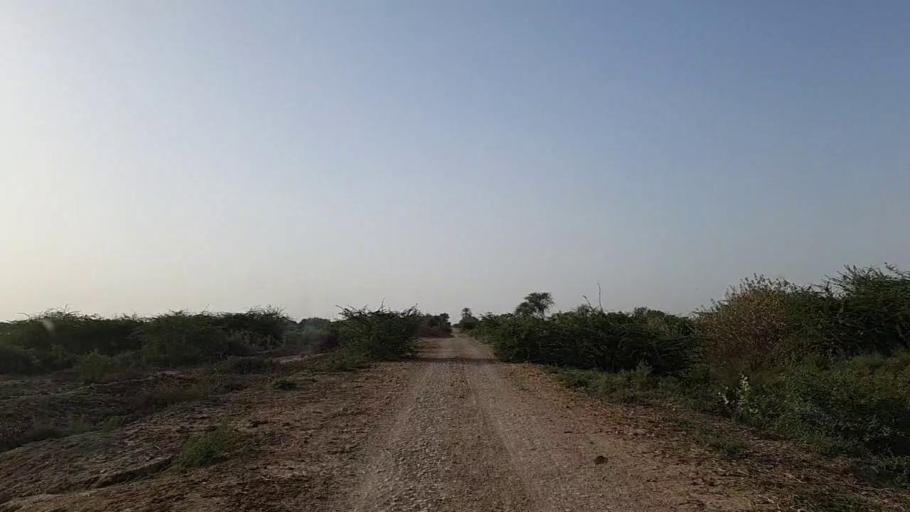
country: PK
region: Sindh
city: Jati
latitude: 24.3429
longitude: 68.1460
